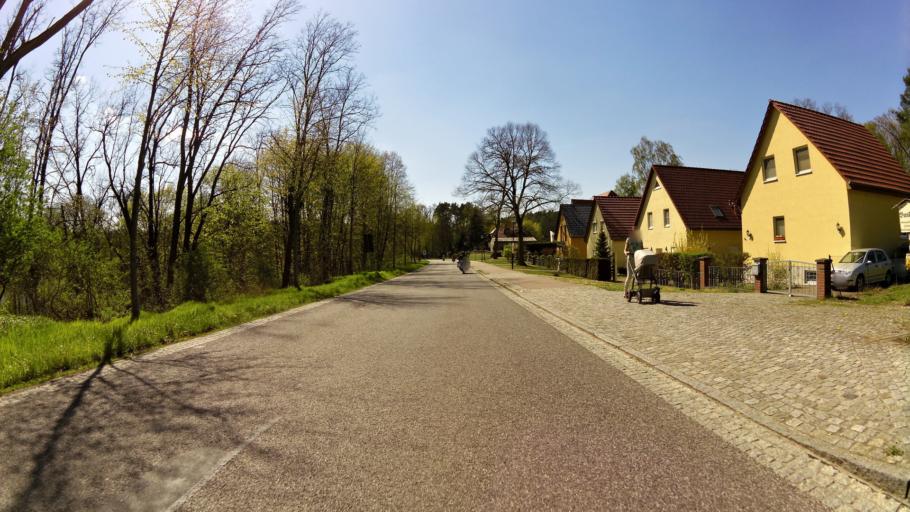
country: DE
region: Brandenburg
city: Waldsieversdorf
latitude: 52.5571
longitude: 14.0663
